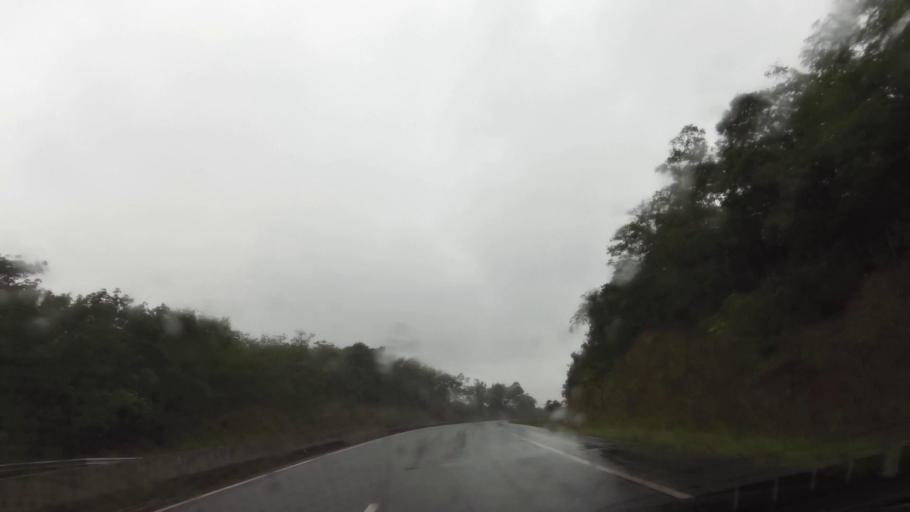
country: BR
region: Espirito Santo
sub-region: Guarapari
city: Guarapari
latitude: -20.6288
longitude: -40.5077
